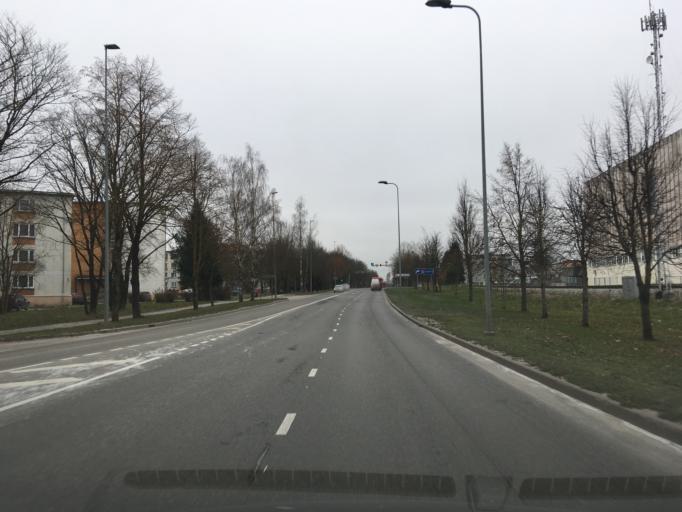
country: EE
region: Ida-Virumaa
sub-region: Johvi vald
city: Johvi
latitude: 59.3534
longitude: 27.4154
